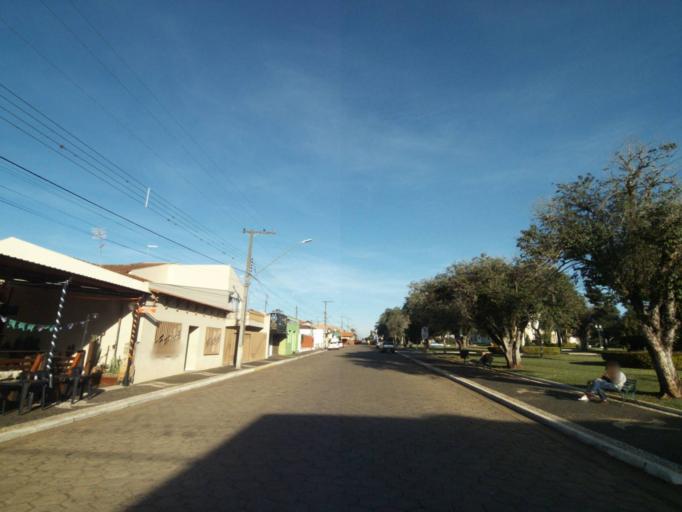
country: BR
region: Parana
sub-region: Tibagi
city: Tibagi
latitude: -24.5142
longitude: -50.4104
